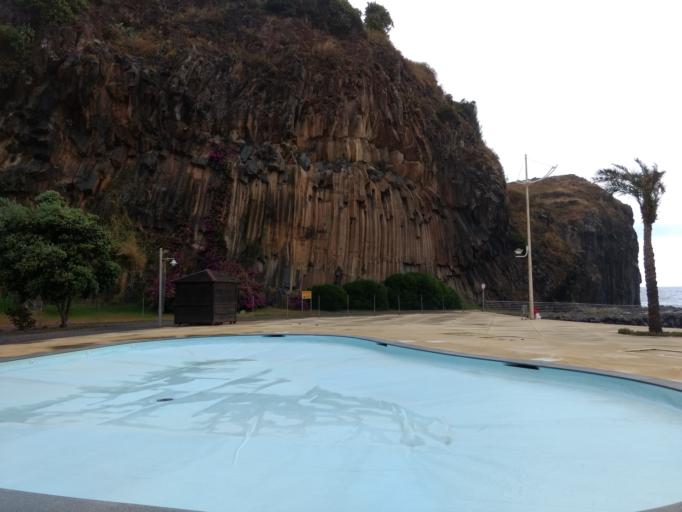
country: PT
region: Madeira
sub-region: Santana
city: Santana
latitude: 32.7928
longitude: -16.8494
